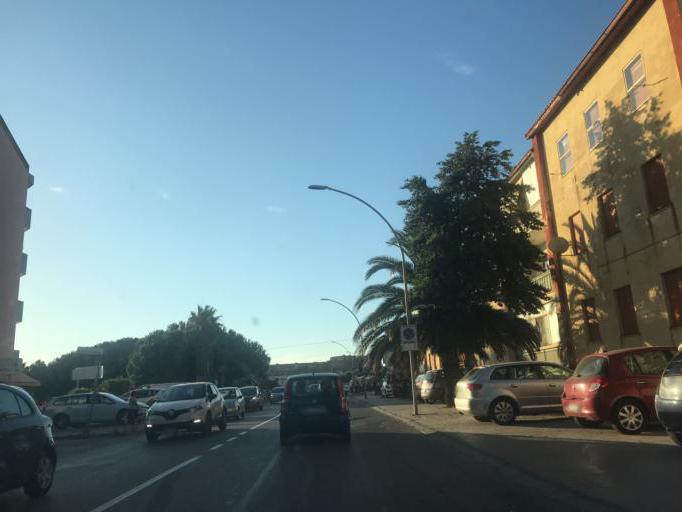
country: IT
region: Sardinia
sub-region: Provincia di Sassari
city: Alghero
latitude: 40.5766
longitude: 8.3202
